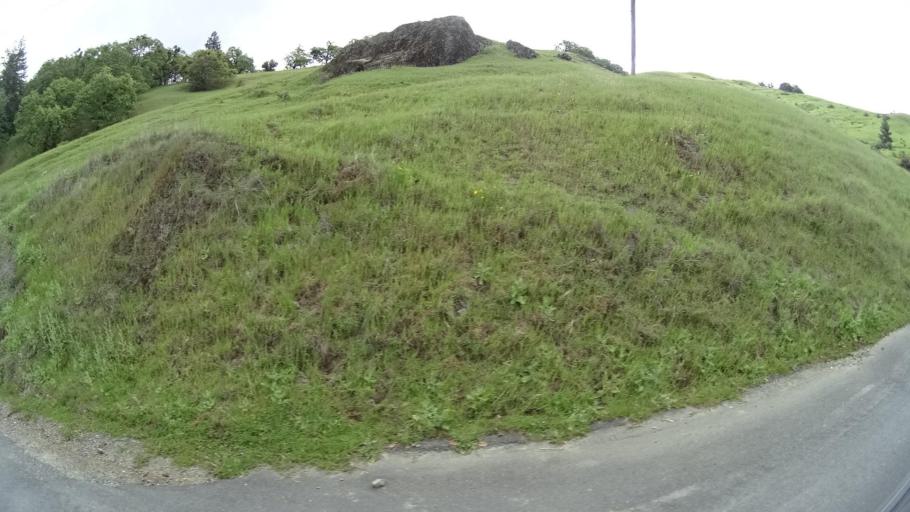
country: US
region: California
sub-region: Humboldt County
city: Redway
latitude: 40.1792
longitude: -123.5717
